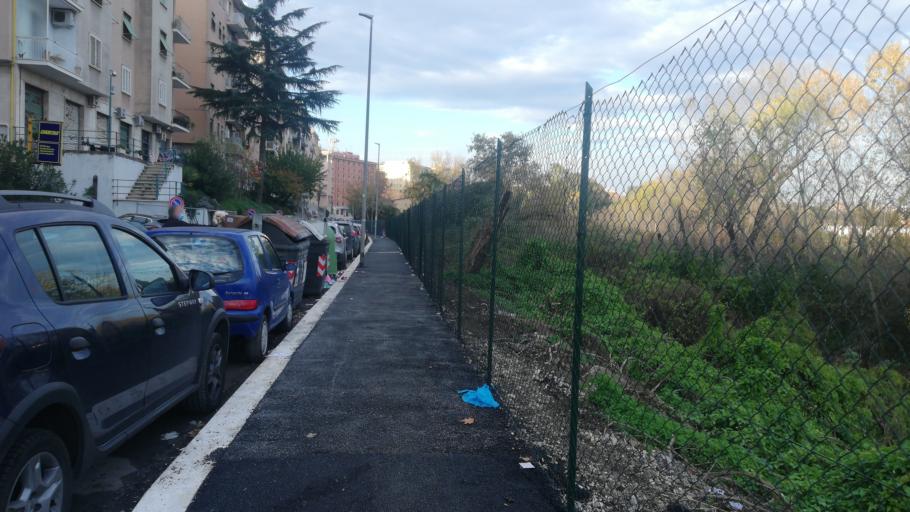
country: IT
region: Latium
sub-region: Citta metropolitana di Roma Capitale
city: Rome
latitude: 41.9300
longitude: 12.5288
